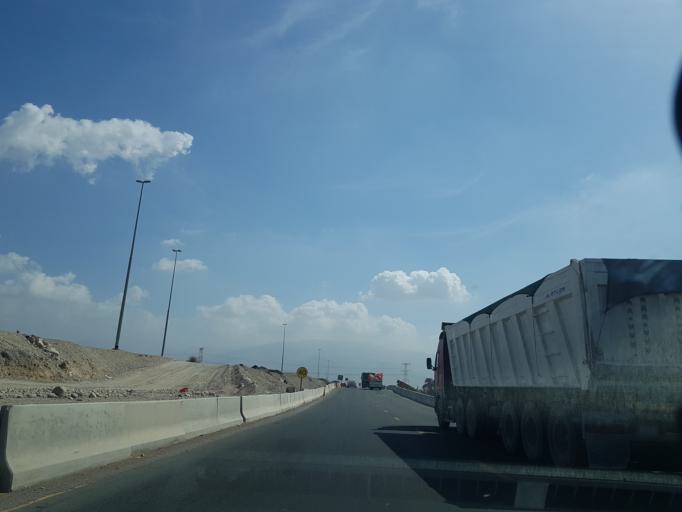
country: AE
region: Ra's al Khaymah
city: Ras al-Khaimah
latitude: 25.6985
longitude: 55.9710
